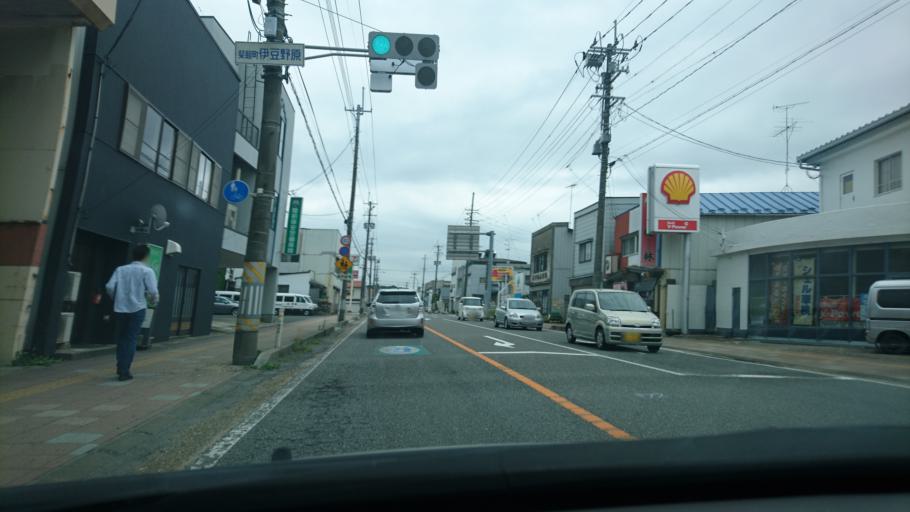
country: JP
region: Miyagi
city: Furukawa
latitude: 38.7349
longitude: 141.0224
